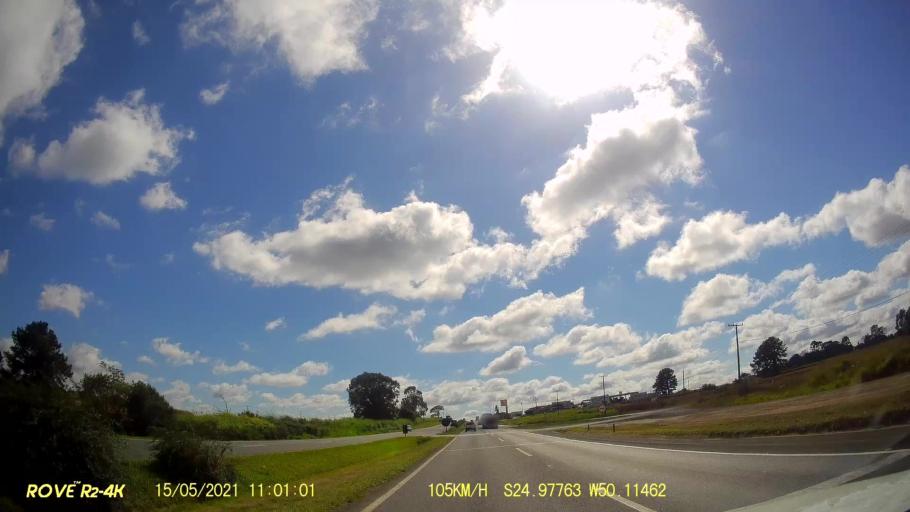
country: BR
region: Parana
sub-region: Carambei
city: Carambei
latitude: -24.9775
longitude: -50.1148
